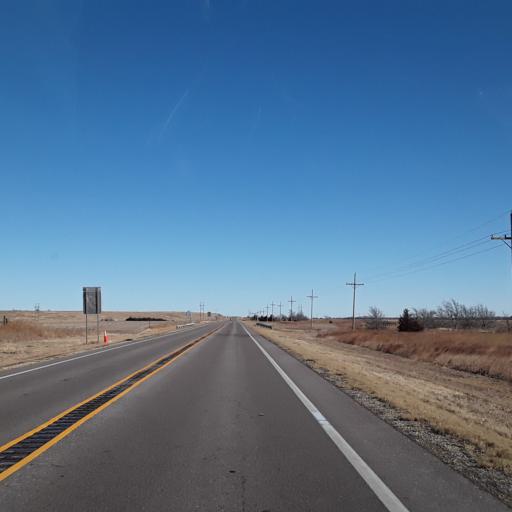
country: US
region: Kansas
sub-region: Pawnee County
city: Larned
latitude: 38.0824
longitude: -99.2333
